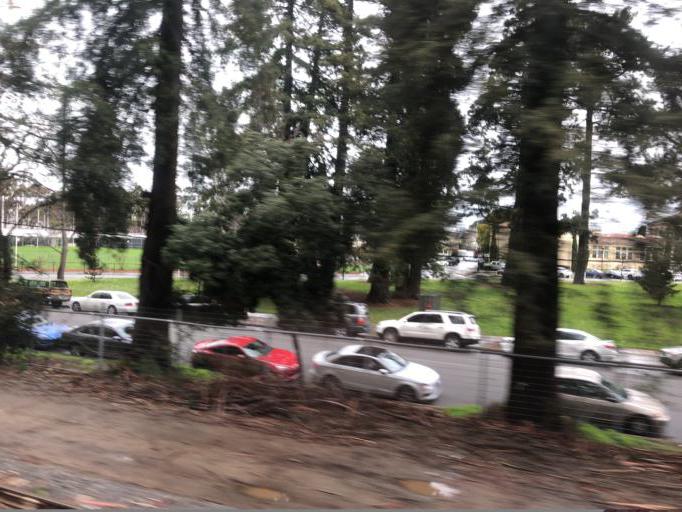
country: US
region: California
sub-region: San Mateo County
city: Burlingame
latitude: 37.5814
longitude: -122.3478
